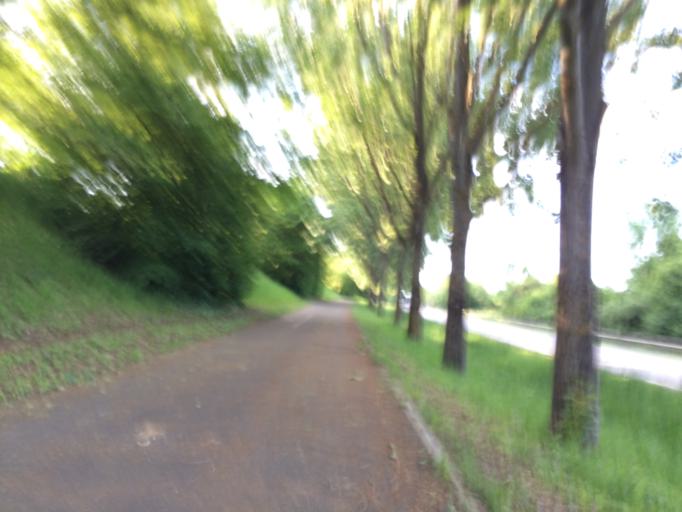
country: FR
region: Ile-de-France
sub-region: Departement de l'Essonne
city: Lisses
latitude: 48.6081
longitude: 2.4250
